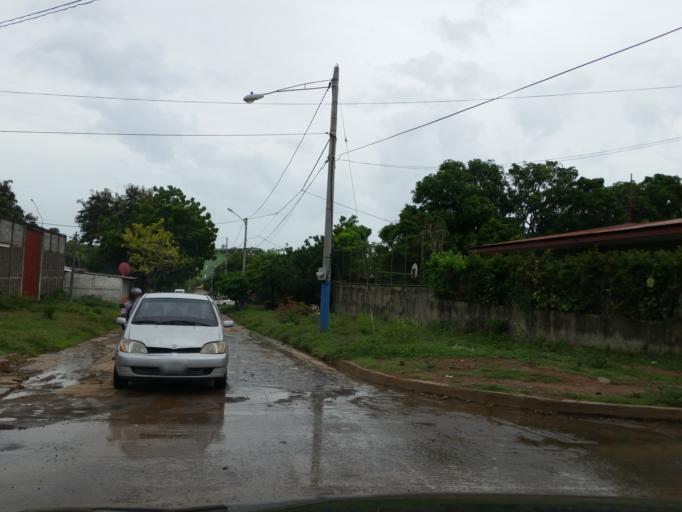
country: NI
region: Granada
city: Granada
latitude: 11.9383
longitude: -85.9621
